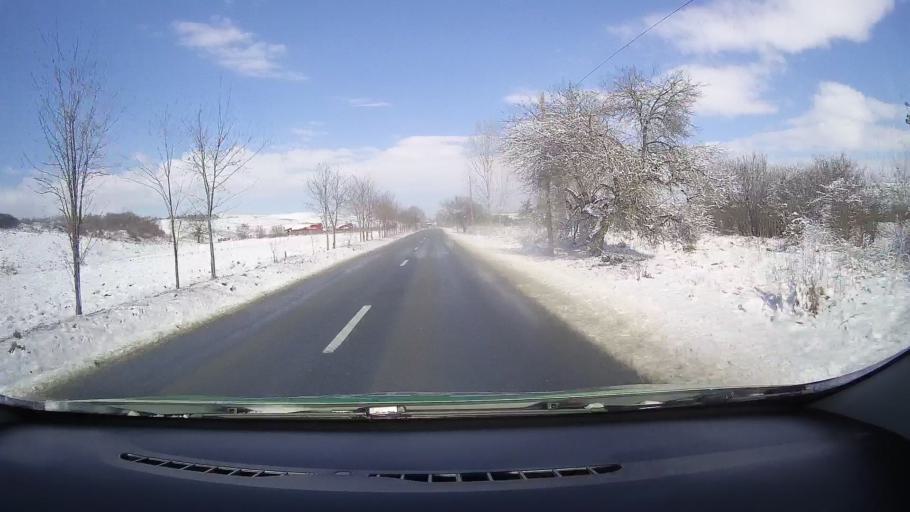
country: RO
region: Sibiu
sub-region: Comuna Nocrich
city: Nocrich
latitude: 45.8747
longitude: 24.4513
